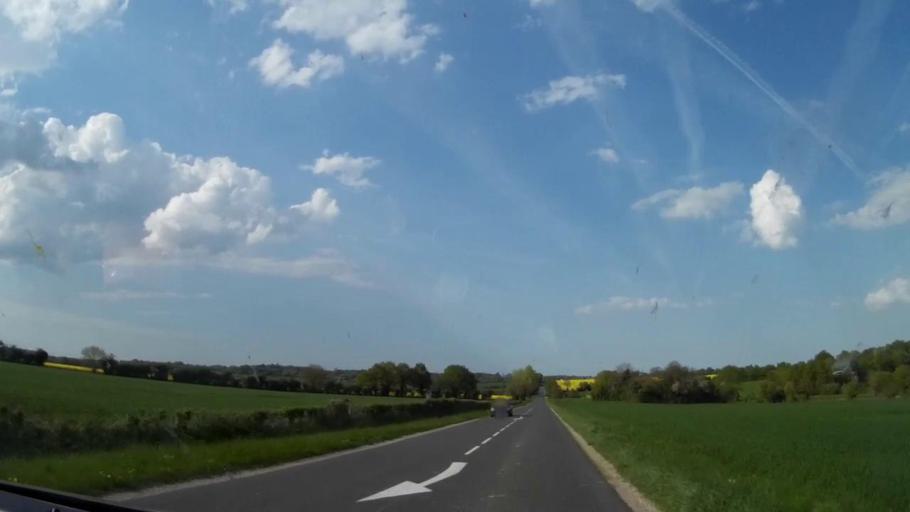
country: FR
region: Centre
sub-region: Departement du Loir-et-Cher
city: Mondoubleau
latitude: 47.9159
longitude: 0.9315
